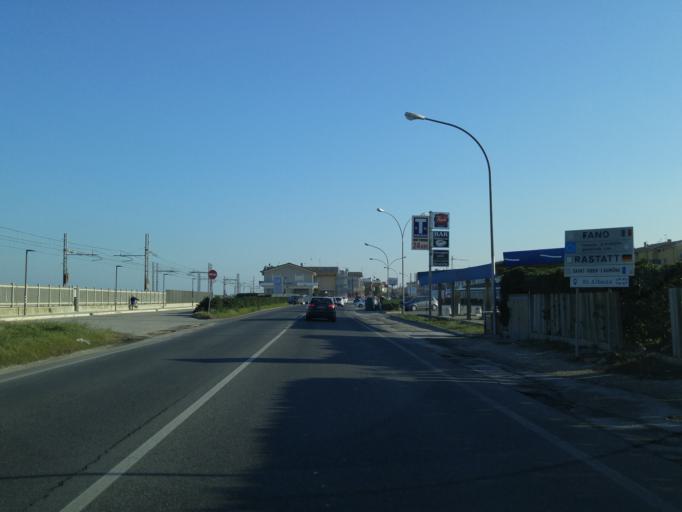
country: IT
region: The Marches
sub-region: Provincia di Pesaro e Urbino
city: Centinarola
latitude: 43.8619
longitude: 12.9911
